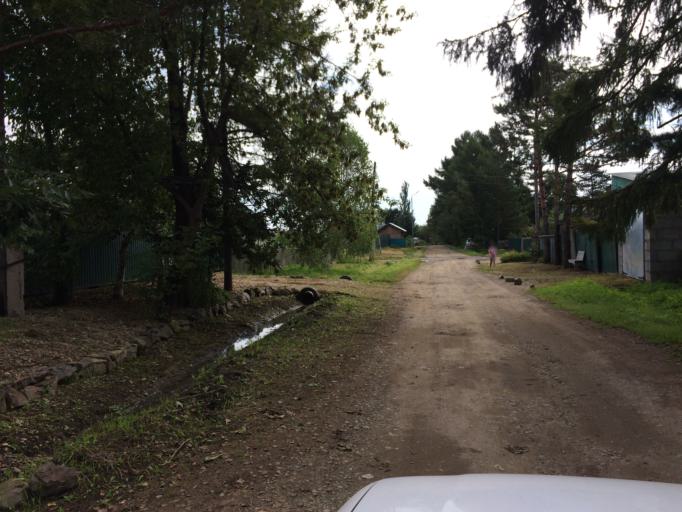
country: RU
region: Primorskiy
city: Dal'nerechensk
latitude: 45.9179
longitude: 133.7133
